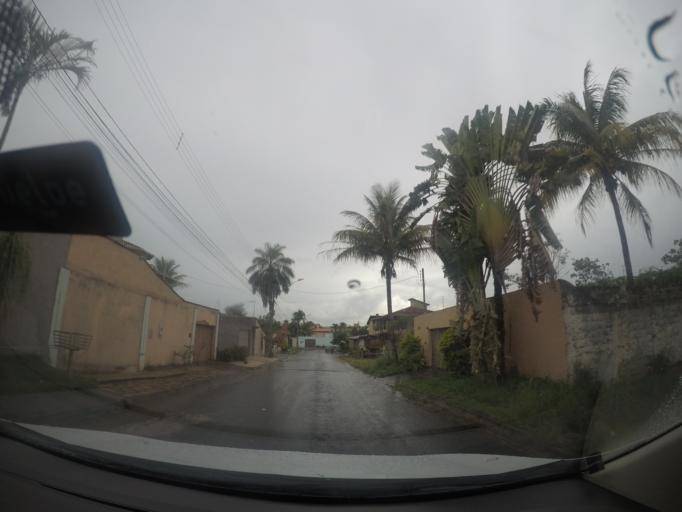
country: BR
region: Goias
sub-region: Goiania
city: Goiania
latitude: -16.6449
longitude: -49.2292
